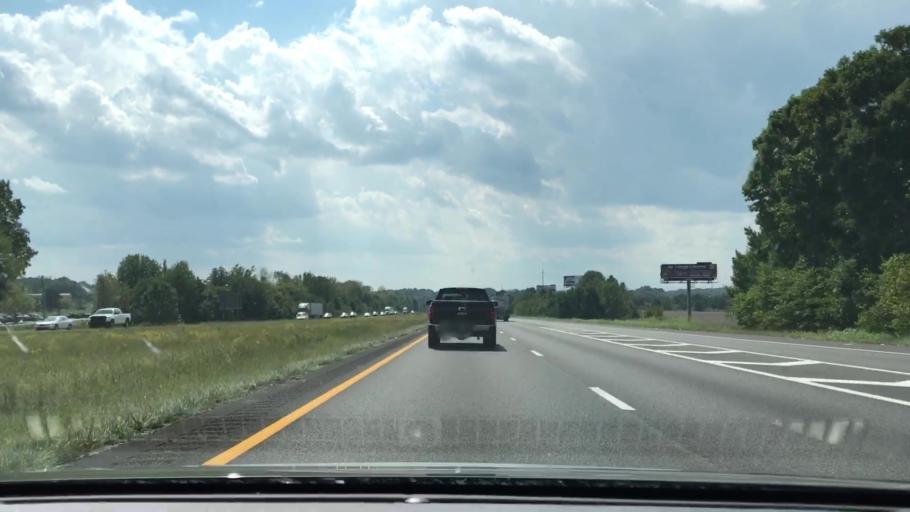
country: US
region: Tennessee
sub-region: Sumner County
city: White House
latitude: 36.4654
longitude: -86.6860
